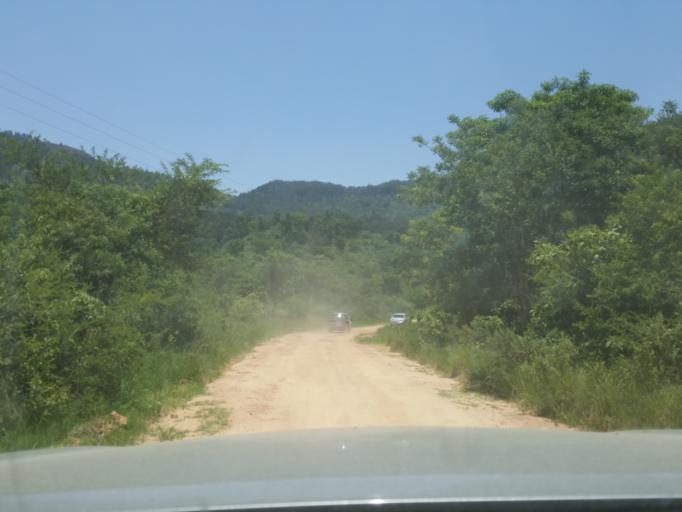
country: ZA
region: Limpopo
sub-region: Mopani District Municipality
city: Hoedspruit
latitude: -24.5967
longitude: 30.8896
